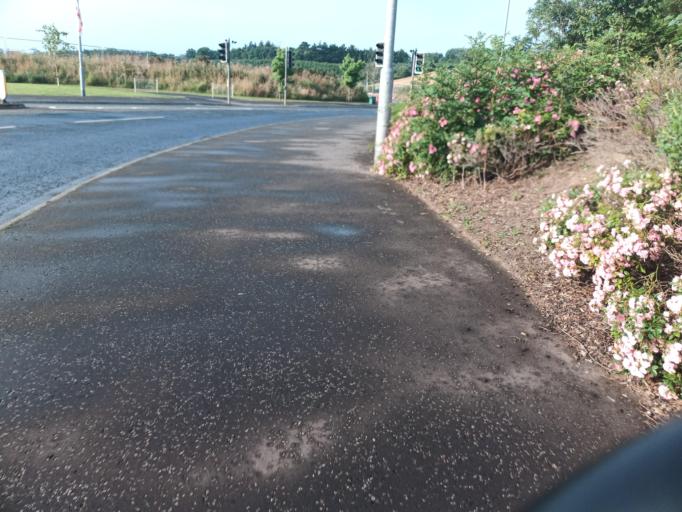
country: GB
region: Northern Ireland
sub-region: Castlereagh District
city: Dundonald
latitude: 54.5827
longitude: -5.7914
